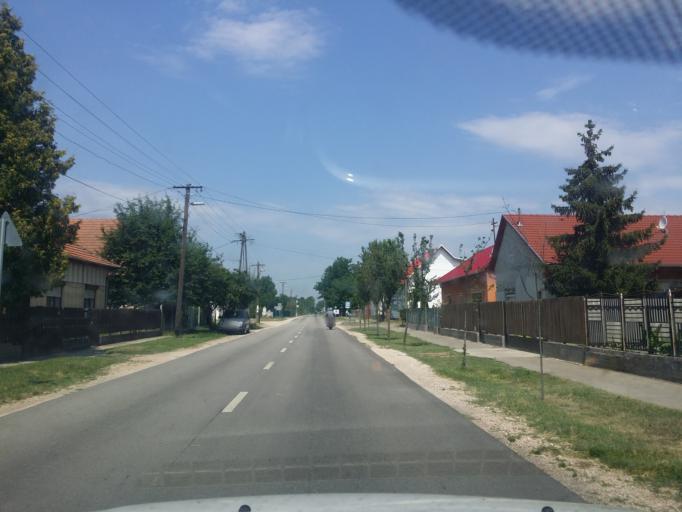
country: HU
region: Bacs-Kiskun
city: Jaszszentlaszlo
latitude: 46.5734
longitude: 19.7482
